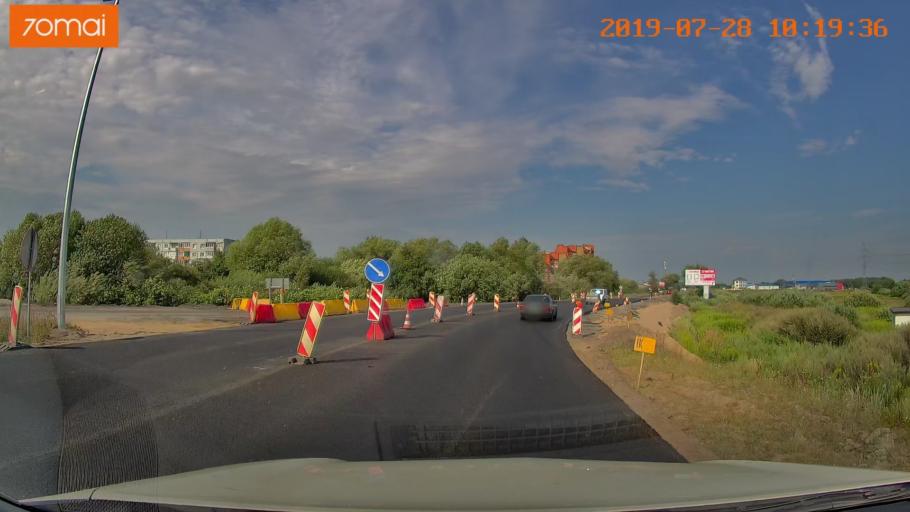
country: RU
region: Kaliningrad
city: Maloye Isakovo
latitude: 54.7481
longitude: 20.5859
